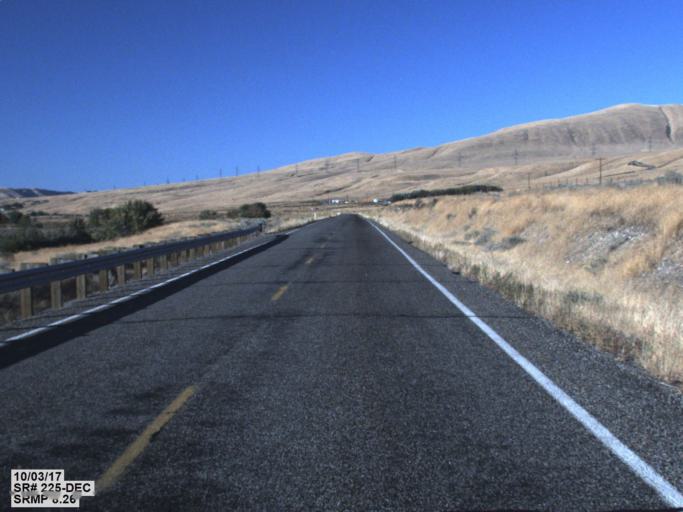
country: US
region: Washington
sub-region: Benton County
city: Benton City
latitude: 46.3529
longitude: -119.4593
